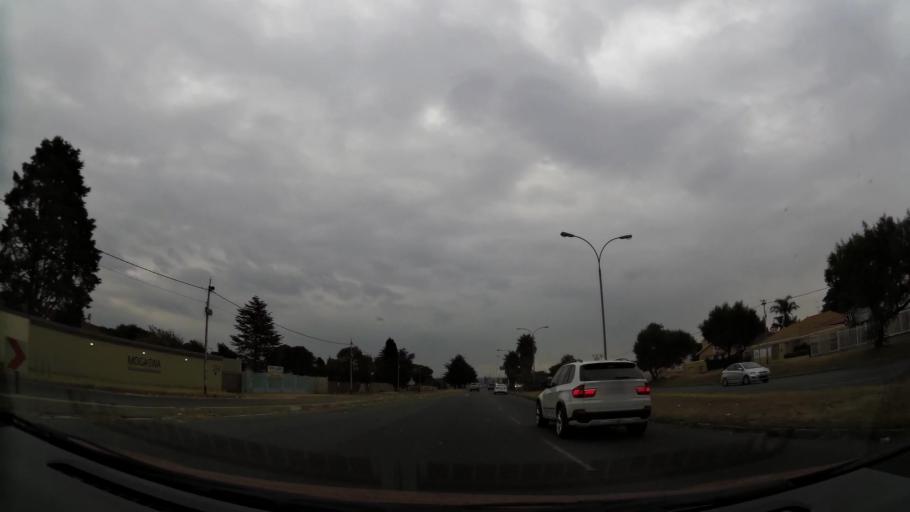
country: ZA
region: Gauteng
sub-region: City of Johannesburg Metropolitan Municipality
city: Roodepoort
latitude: -26.1451
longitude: 27.8796
